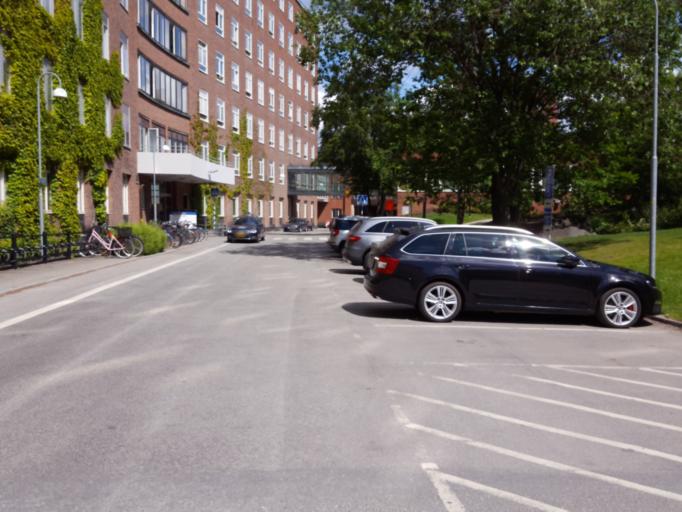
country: SE
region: Stockholm
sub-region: Norrtalje Kommun
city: Bergshamra
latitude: 59.3514
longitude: 18.0330
